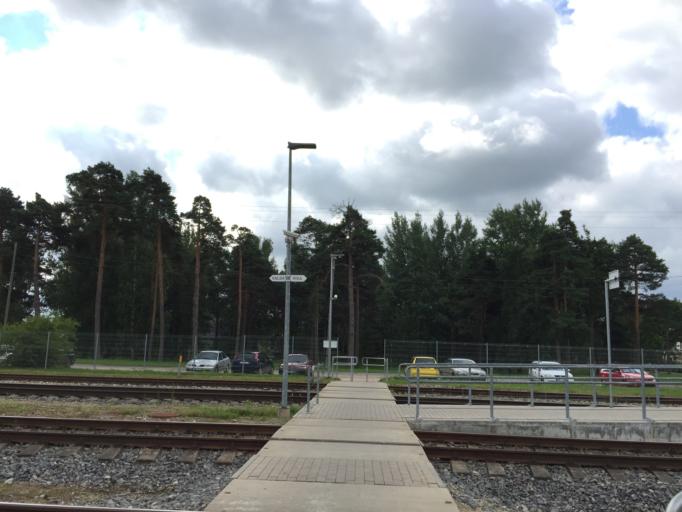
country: LV
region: Sigulda
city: Sigulda
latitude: 57.1534
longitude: 24.8564
